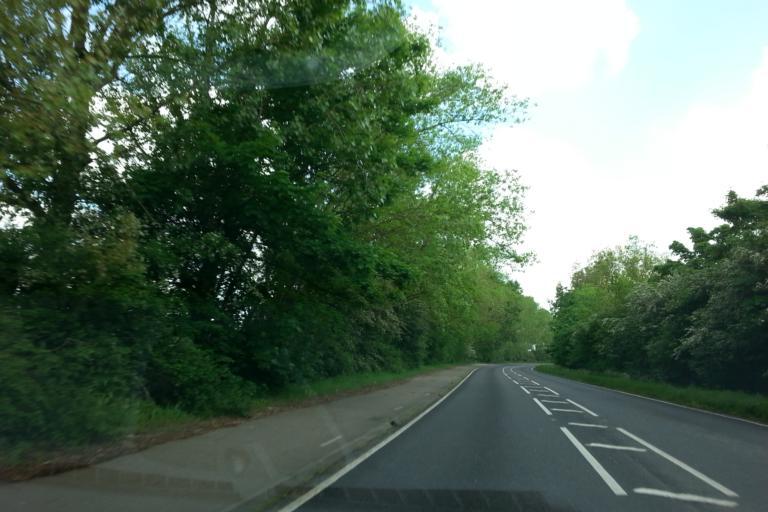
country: GB
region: England
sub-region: Cambridgeshire
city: Stilton
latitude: 52.5078
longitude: -0.2812
